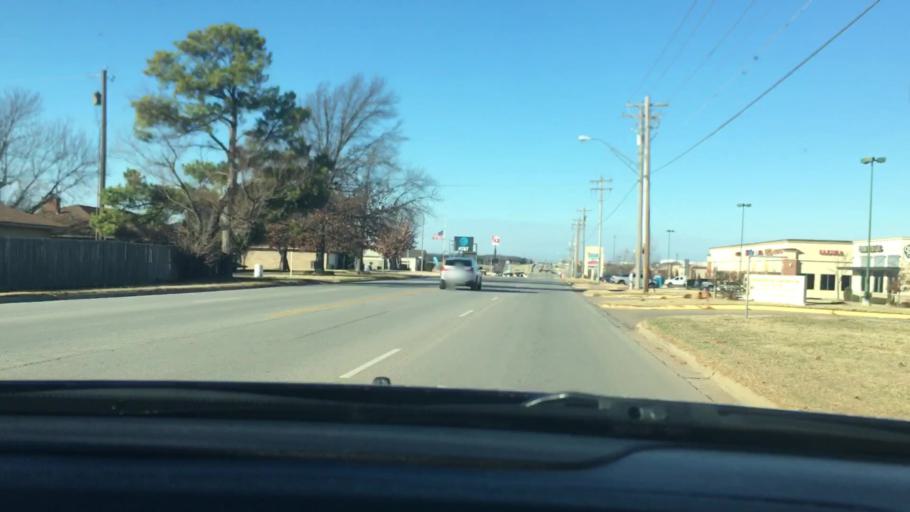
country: US
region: Oklahoma
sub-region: Carter County
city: Ardmore
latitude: 34.1875
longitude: -97.1556
